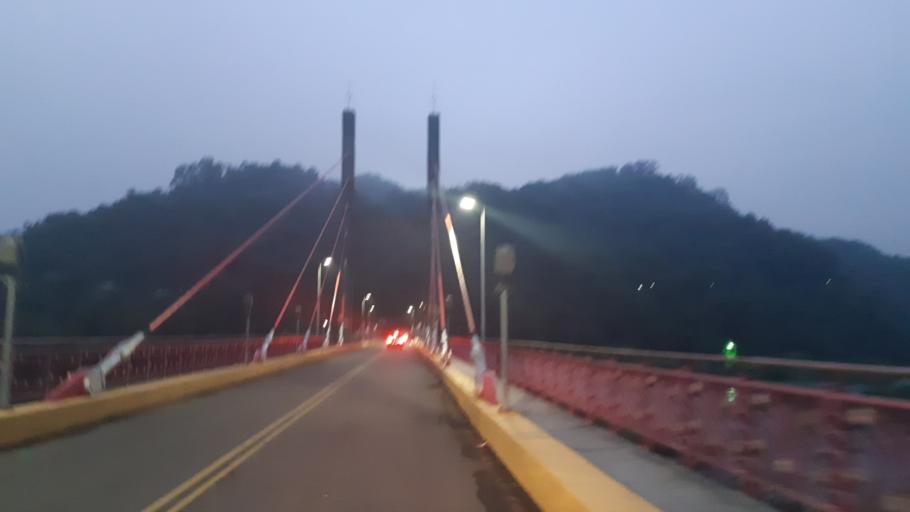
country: TW
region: Taiwan
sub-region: Hsinchu
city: Zhubei
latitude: 24.7051
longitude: 121.1480
